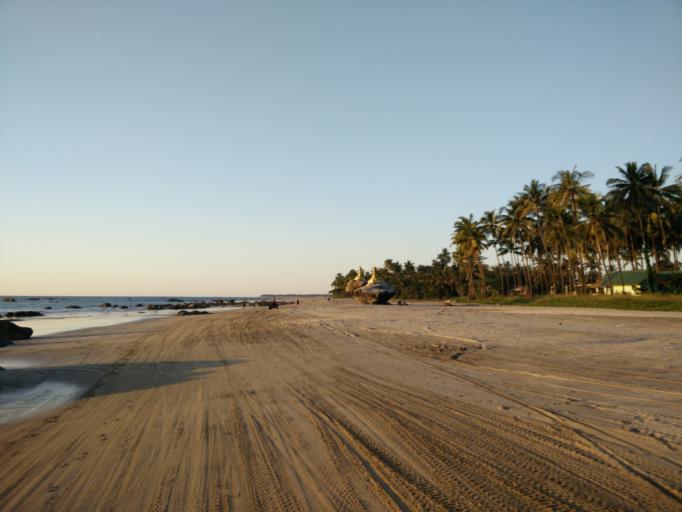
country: MM
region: Ayeyarwady
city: Pathein
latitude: 16.8333
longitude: 94.3932
